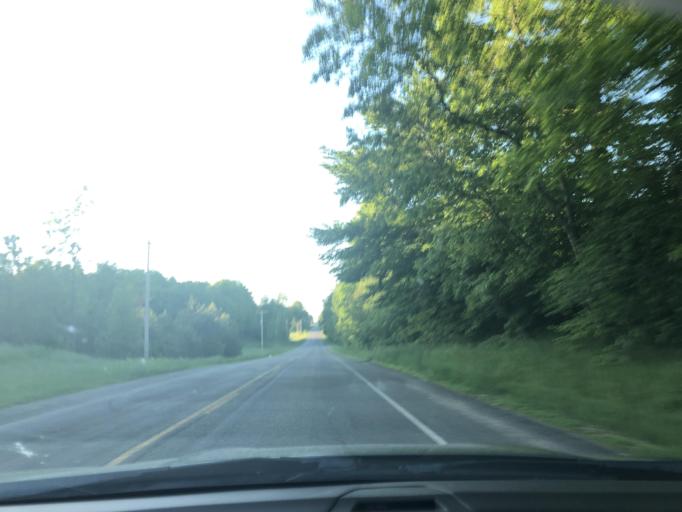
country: US
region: Michigan
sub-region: Missaukee County
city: Lake City
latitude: 44.4542
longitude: -85.0746
